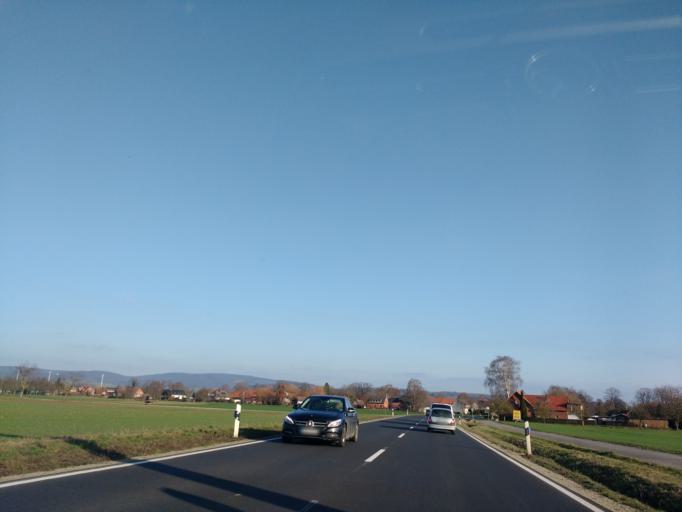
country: DE
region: Lower Saxony
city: Hessisch Oldendorf
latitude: 52.1387
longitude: 9.2637
